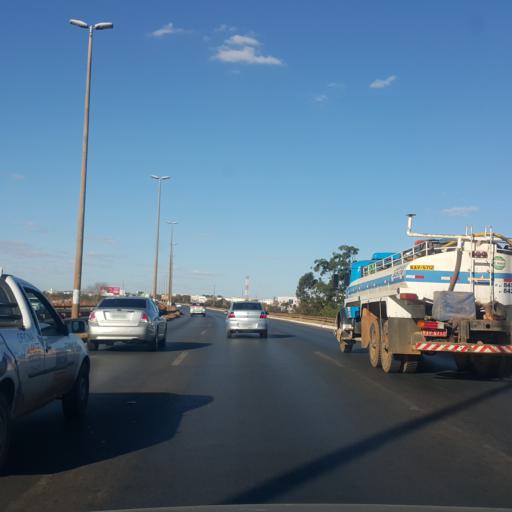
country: BR
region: Federal District
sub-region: Brasilia
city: Brasilia
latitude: -15.7959
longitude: -47.9672
